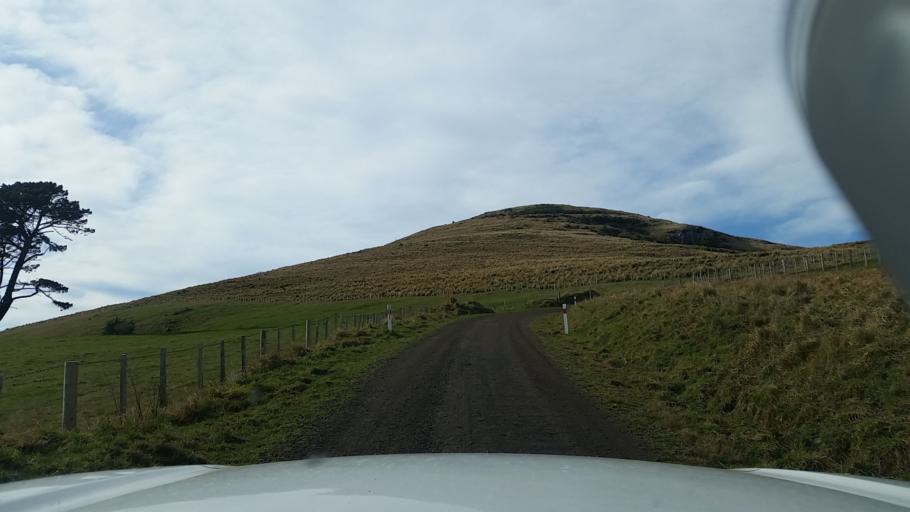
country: NZ
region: Canterbury
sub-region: Christchurch City
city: Christchurch
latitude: -43.6756
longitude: 172.8487
